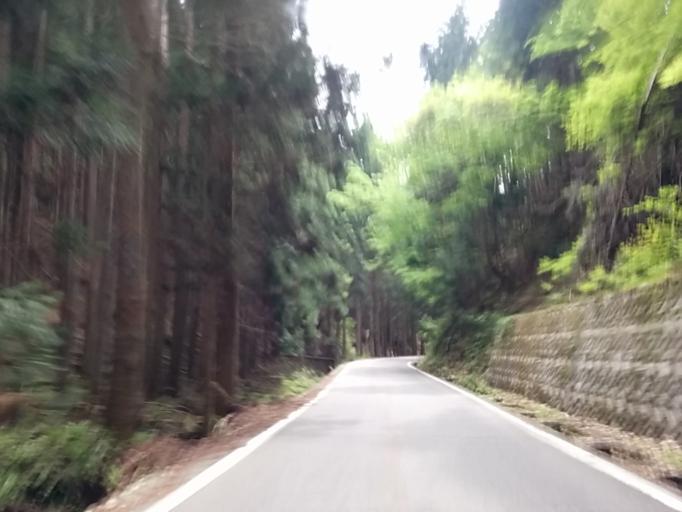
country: JP
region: Gifu
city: Gujo
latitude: 35.7312
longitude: 136.9690
